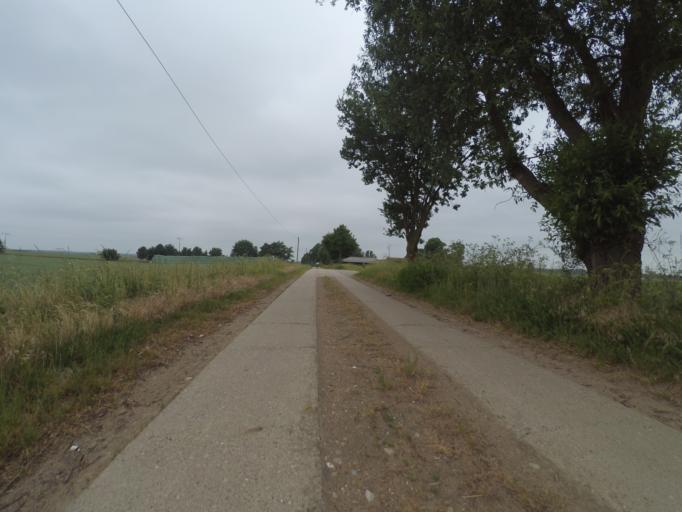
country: DE
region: Mecklenburg-Vorpommern
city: Dabel
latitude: 53.6712
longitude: 11.9280
